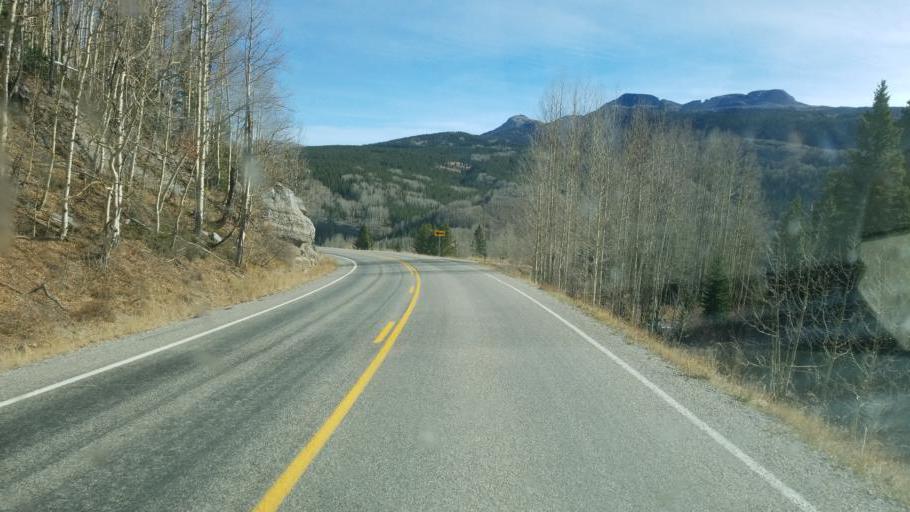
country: US
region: Colorado
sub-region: San Juan County
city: Silverton
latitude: 37.7119
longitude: -107.7585
